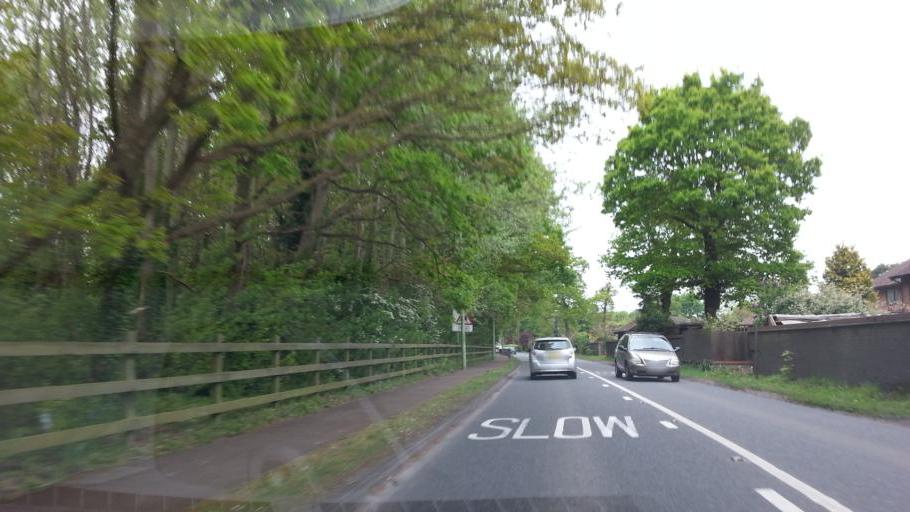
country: GB
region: England
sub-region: Suffolk
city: Lakenheath
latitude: 52.3429
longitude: 0.5271
